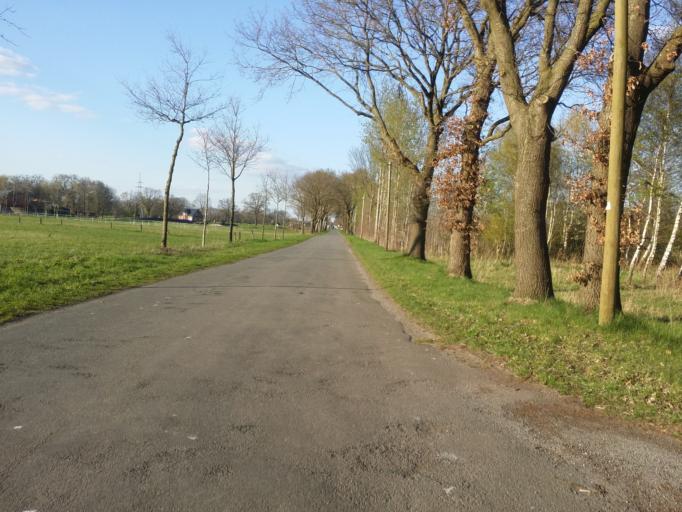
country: DE
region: Lower Saxony
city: Delmenhorst
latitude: 53.0088
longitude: 8.6409
